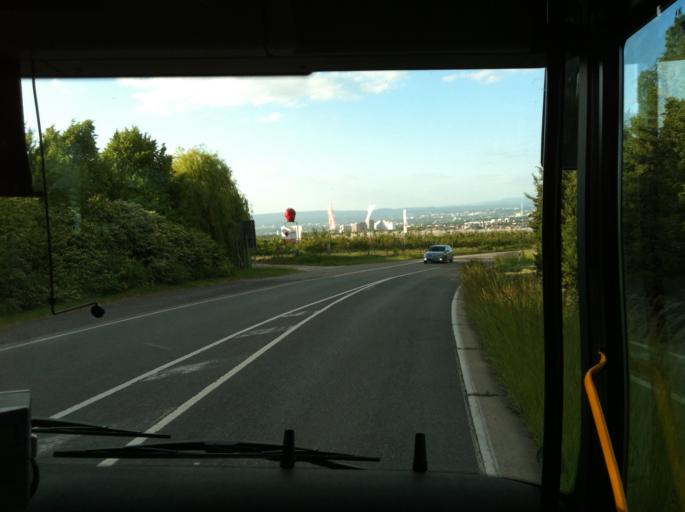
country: DE
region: Rheinland-Pfalz
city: Ober-Olm
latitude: 49.9808
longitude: 8.1930
